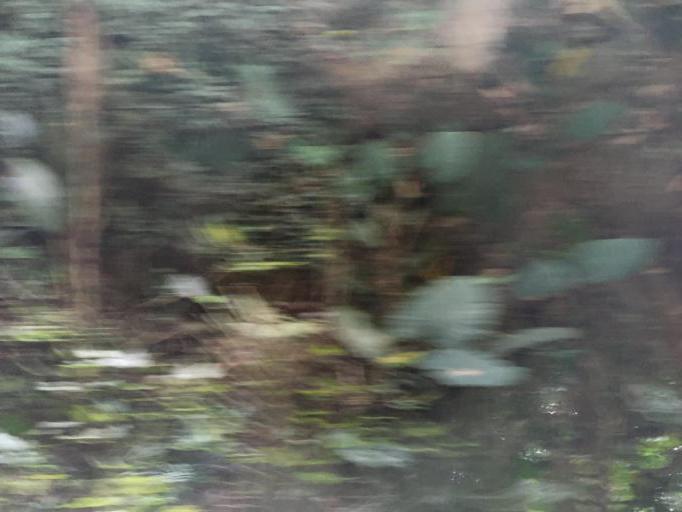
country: TW
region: Taiwan
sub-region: Chiayi
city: Jiayi Shi
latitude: 23.5377
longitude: 120.6069
